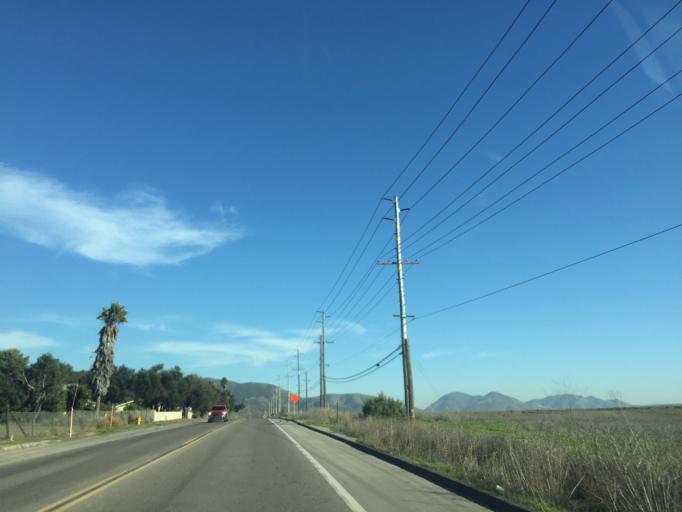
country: MX
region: Baja California
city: Tijuana
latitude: 32.5675
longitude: -116.9358
